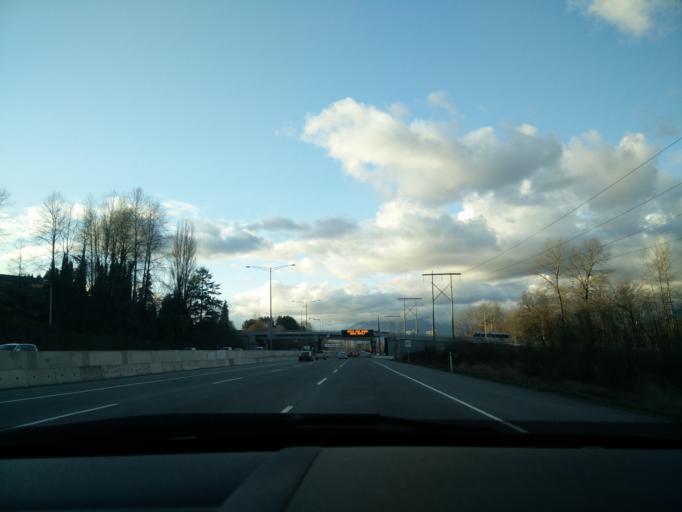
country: CA
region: British Columbia
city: Burnaby
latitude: 49.2482
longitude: -122.9716
